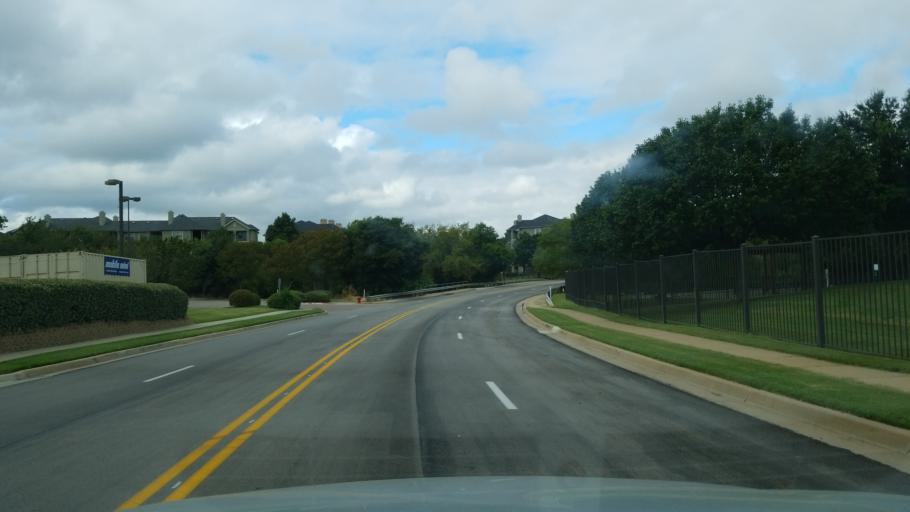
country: US
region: Texas
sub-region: Tarrant County
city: Bedford
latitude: 32.8405
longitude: -97.1228
